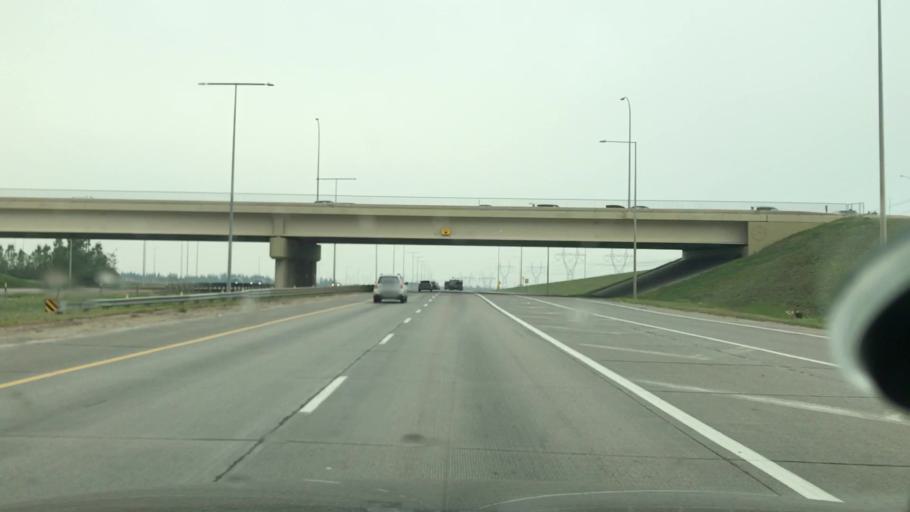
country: CA
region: Alberta
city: Edmonton
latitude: 53.4349
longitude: -113.5178
